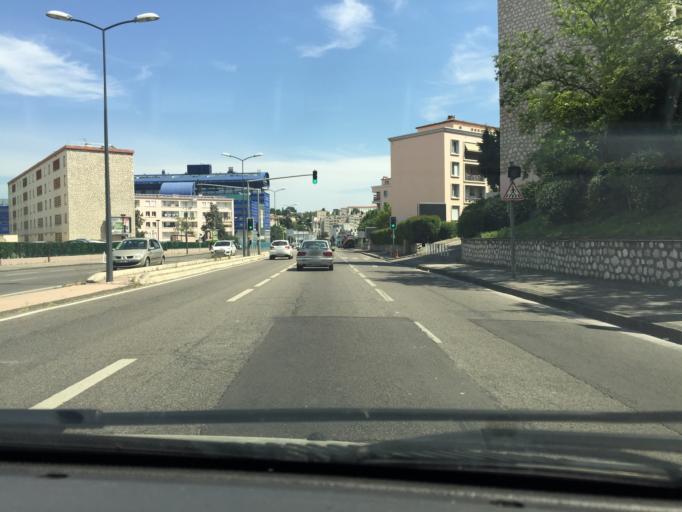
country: FR
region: Provence-Alpes-Cote d'Azur
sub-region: Departement des Bouches-du-Rhone
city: Marseille 13
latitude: 43.3158
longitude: 5.4011
